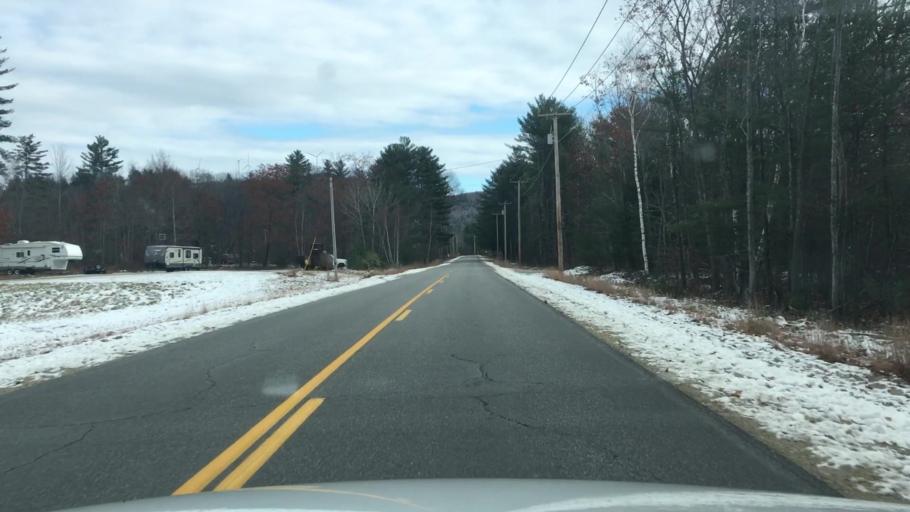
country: US
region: Maine
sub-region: Oxford County
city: Canton
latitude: 44.4897
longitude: -70.3444
